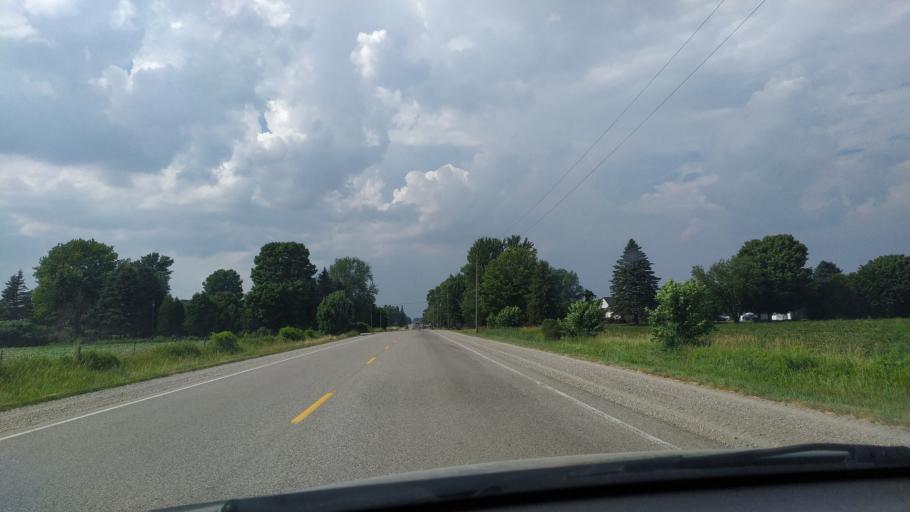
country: CA
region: Ontario
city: Dorchester
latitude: 43.0365
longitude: -81.1236
